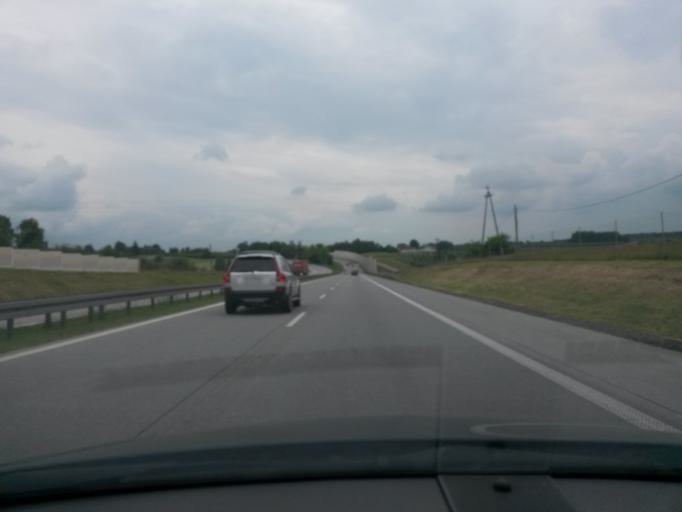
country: PL
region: Lodz Voivodeship
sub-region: Powiat skierniewicki
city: Kowiesy
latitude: 51.8794
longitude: 20.3962
